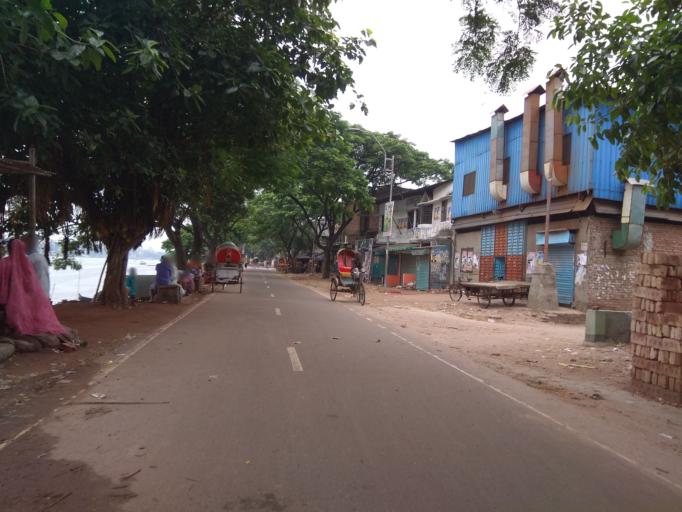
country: BD
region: Dhaka
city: Azimpur
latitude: 23.7092
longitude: 90.3850
